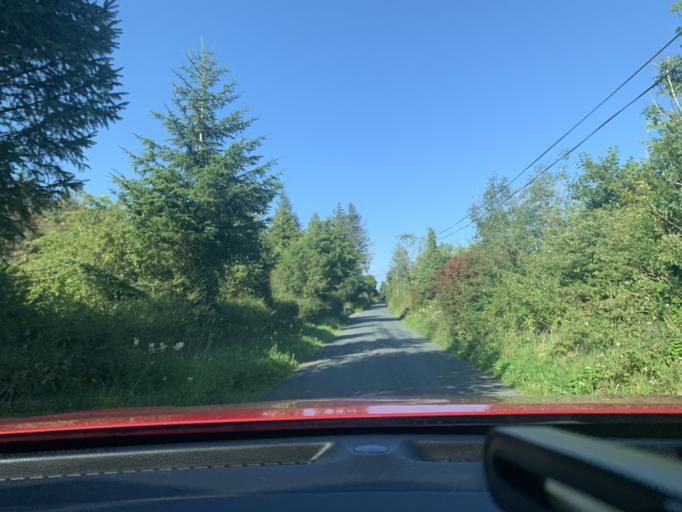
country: IE
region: Connaught
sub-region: Sligo
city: Tobercurry
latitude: 54.1184
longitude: -8.7560
